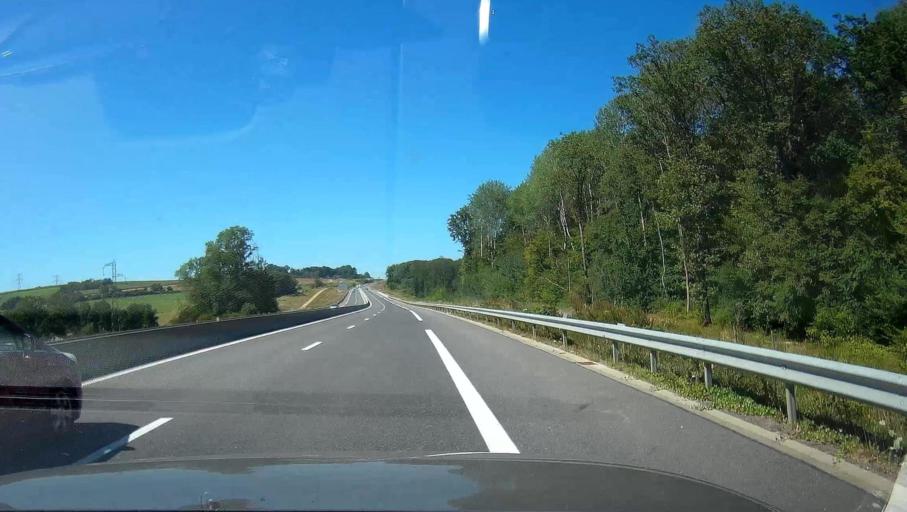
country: FR
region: Champagne-Ardenne
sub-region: Departement des Ardennes
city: Prix-les-Mezieres
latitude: 49.7336
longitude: 4.6891
